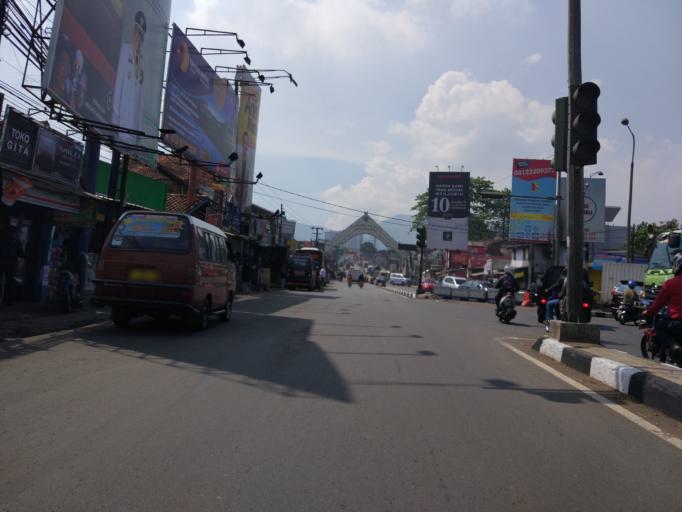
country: ID
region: West Java
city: Cileunyi
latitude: -6.9379
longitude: 107.7564
